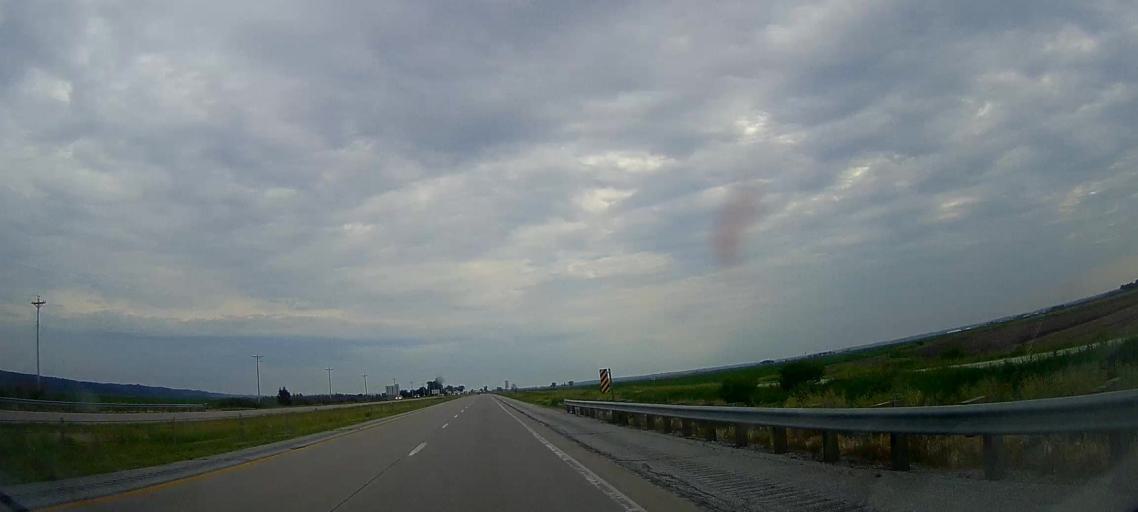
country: US
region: Iowa
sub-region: Harrison County
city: Missouri Valley
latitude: 41.5430
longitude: -95.9177
